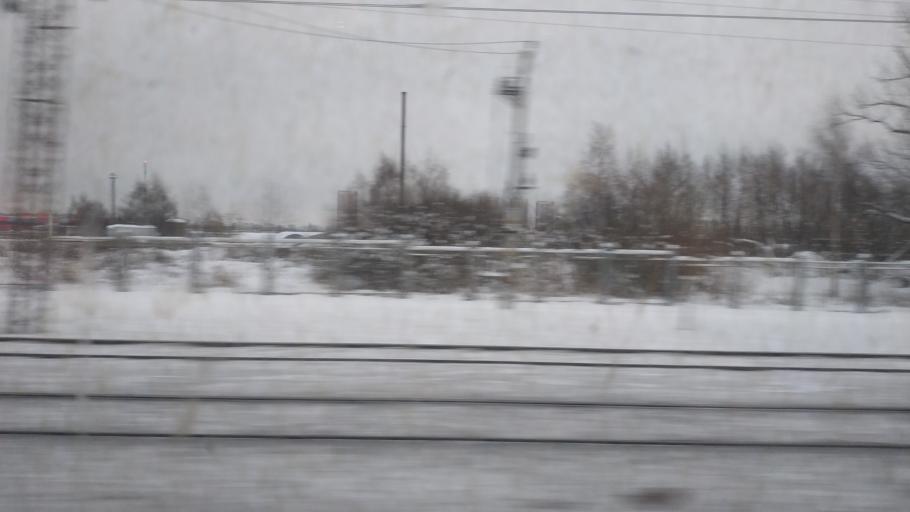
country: RU
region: Moskovskaya
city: Shcherbinka
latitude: 55.5311
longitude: 37.5683
